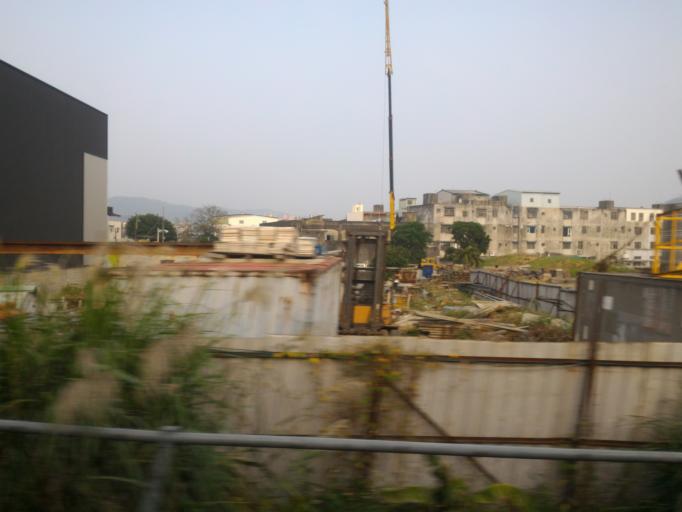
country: TW
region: Taiwan
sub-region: Taoyuan
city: Taoyuan
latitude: 24.9513
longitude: 121.3363
